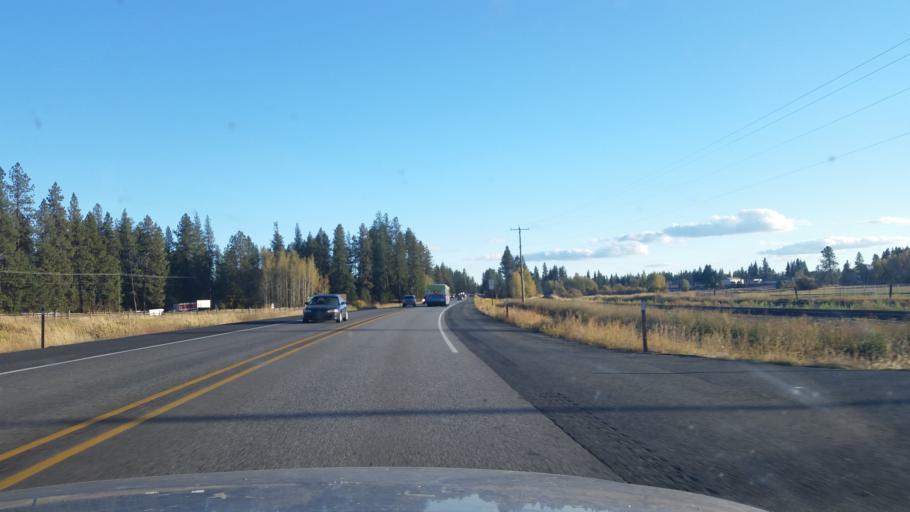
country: US
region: Washington
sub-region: Spokane County
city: Cheney
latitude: 47.5259
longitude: -117.5666
